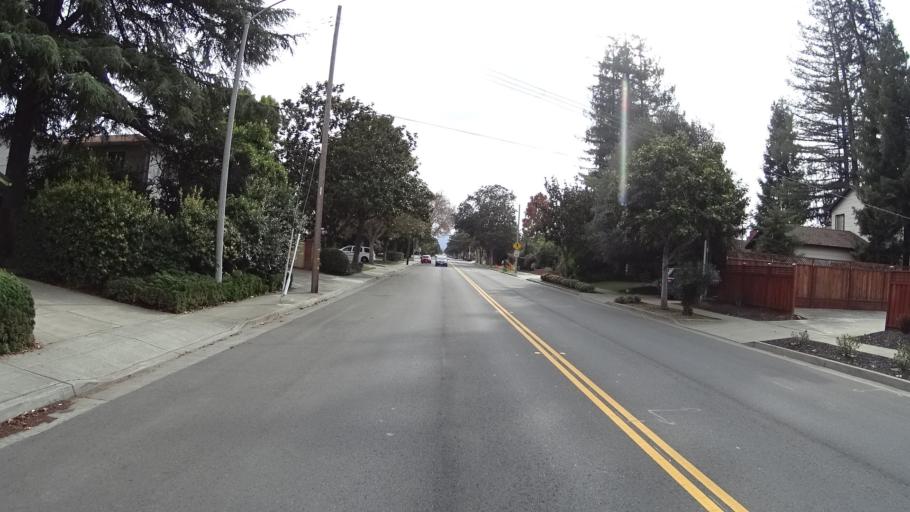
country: US
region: California
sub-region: Santa Clara County
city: Sunnyvale
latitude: 37.3646
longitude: -122.0416
